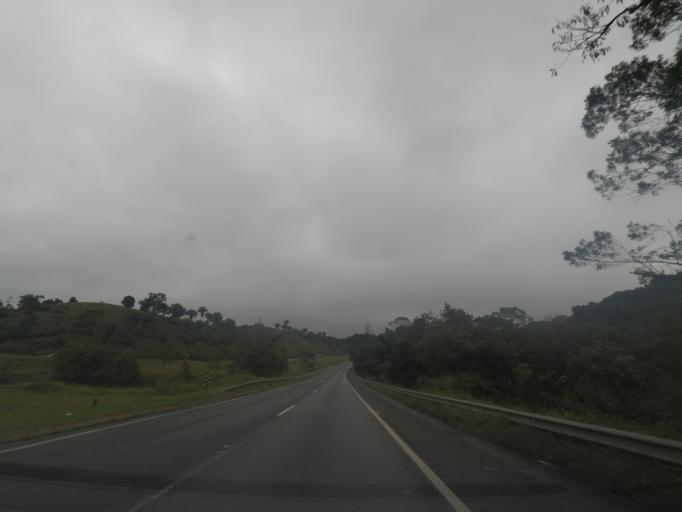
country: BR
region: Parana
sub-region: Antonina
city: Antonina
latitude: -25.0965
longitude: -48.6645
